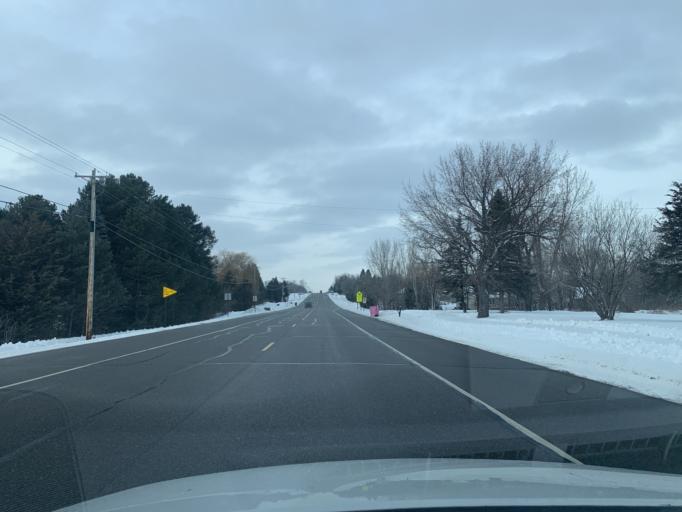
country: US
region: Minnesota
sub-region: Anoka County
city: Anoka
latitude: 45.2389
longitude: -93.4088
